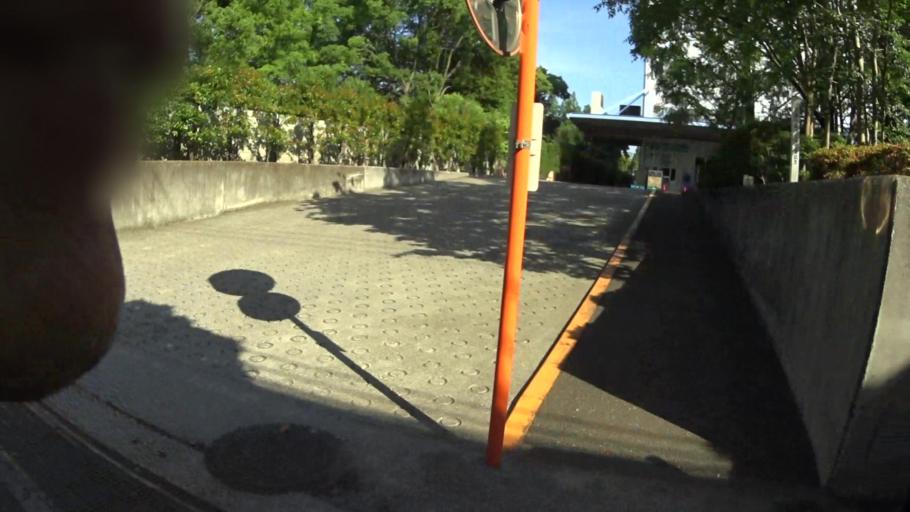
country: JP
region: Kanagawa
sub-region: Kawasaki-shi
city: Kawasaki
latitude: 35.4987
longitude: 139.6920
